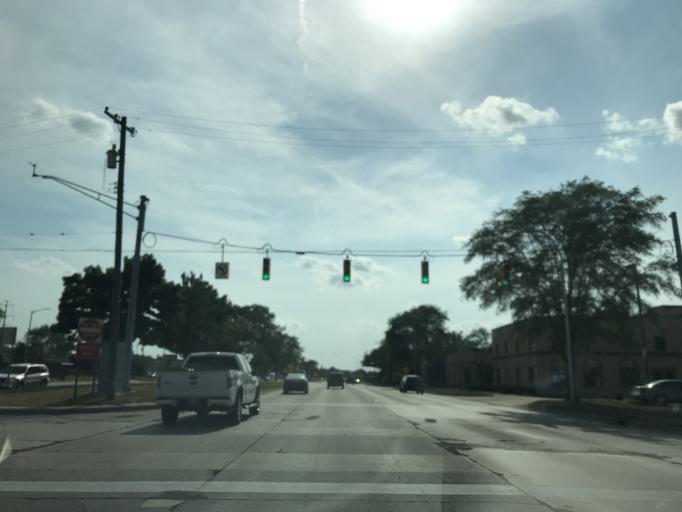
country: US
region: Michigan
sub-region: Wayne County
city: Wayne
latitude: 42.2824
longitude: -83.3701
